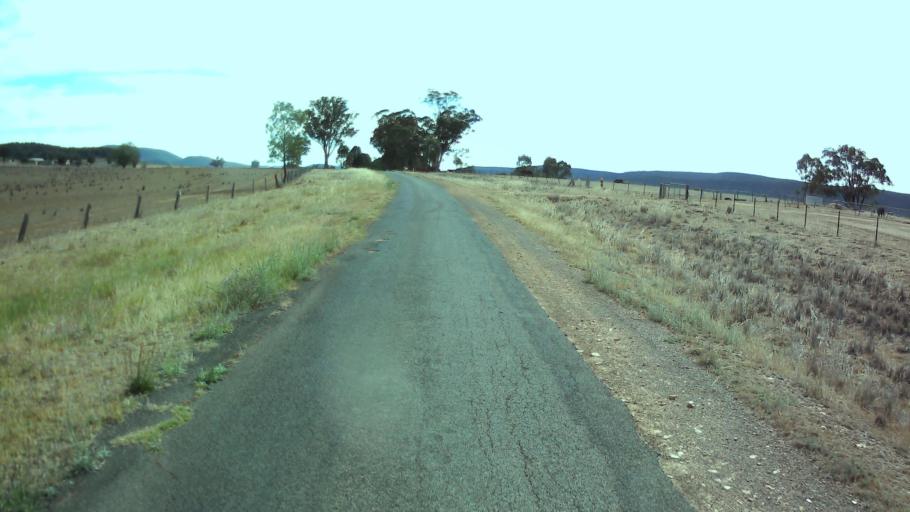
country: AU
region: New South Wales
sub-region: Weddin
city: Grenfell
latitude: -33.8326
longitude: 148.2741
